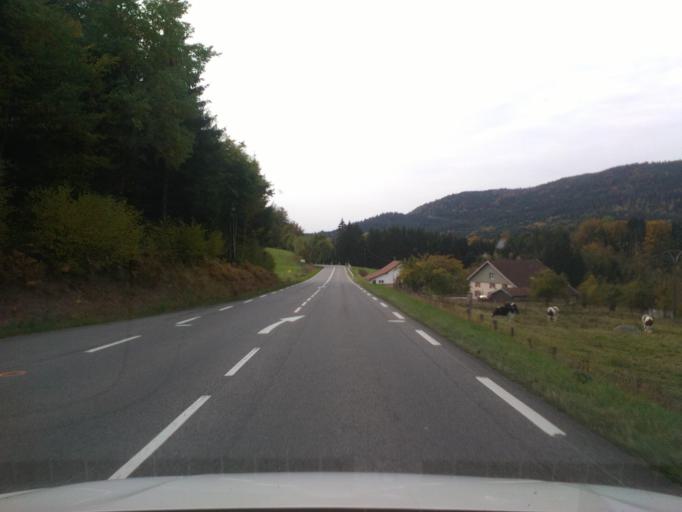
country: FR
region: Lorraine
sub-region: Departement des Vosges
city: Le Syndicat
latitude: 48.0481
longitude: 6.6862
